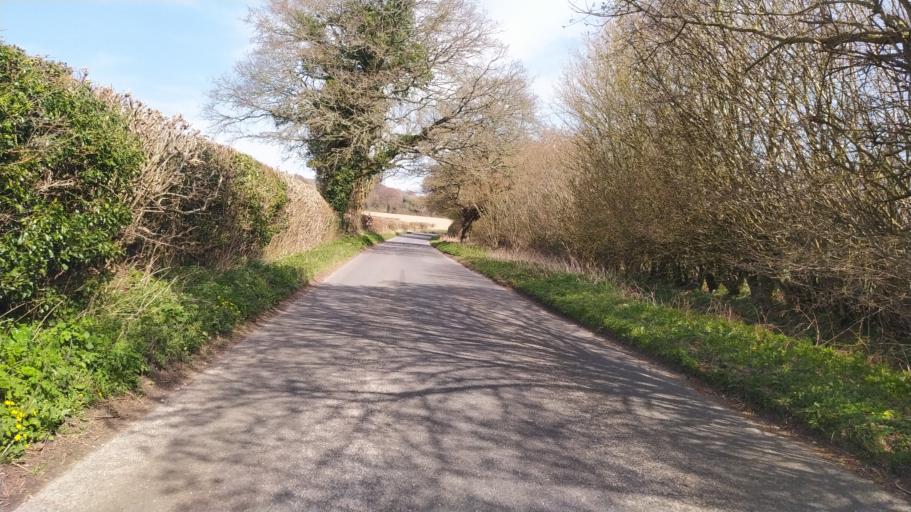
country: GB
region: England
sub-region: Hampshire
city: Four Marks
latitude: 51.0566
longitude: -1.1126
